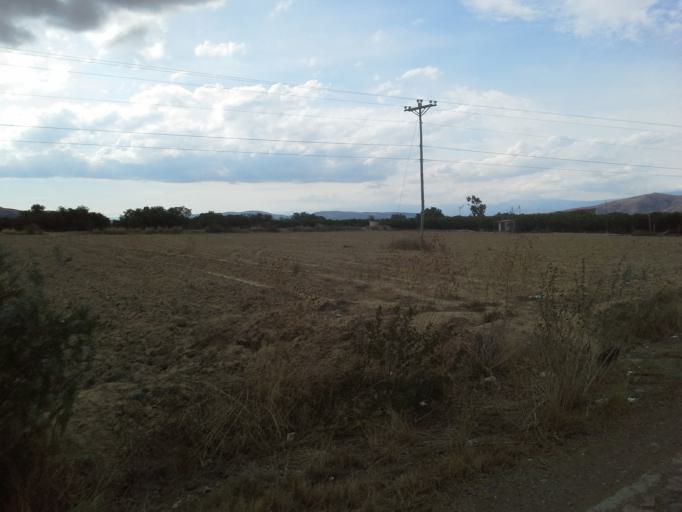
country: BO
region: Cochabamba
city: Tarata
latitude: -17.5895
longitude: -66.0185
